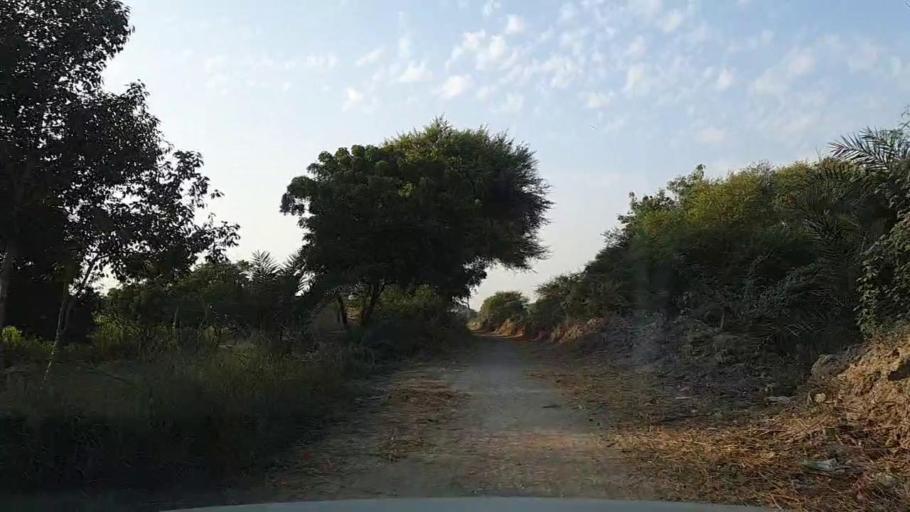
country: PK
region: Sindh
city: Daro Mehar
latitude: 24.7732
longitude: 68.1991
